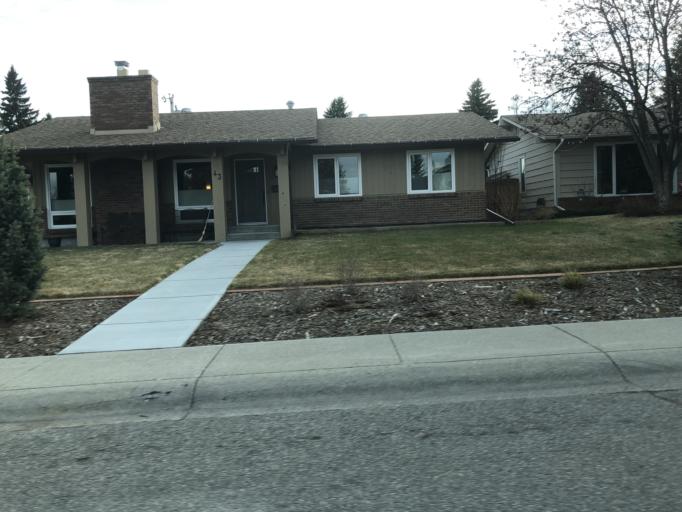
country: CA
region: Alberta
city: Calgary
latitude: 50.9334
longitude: -114.0409
